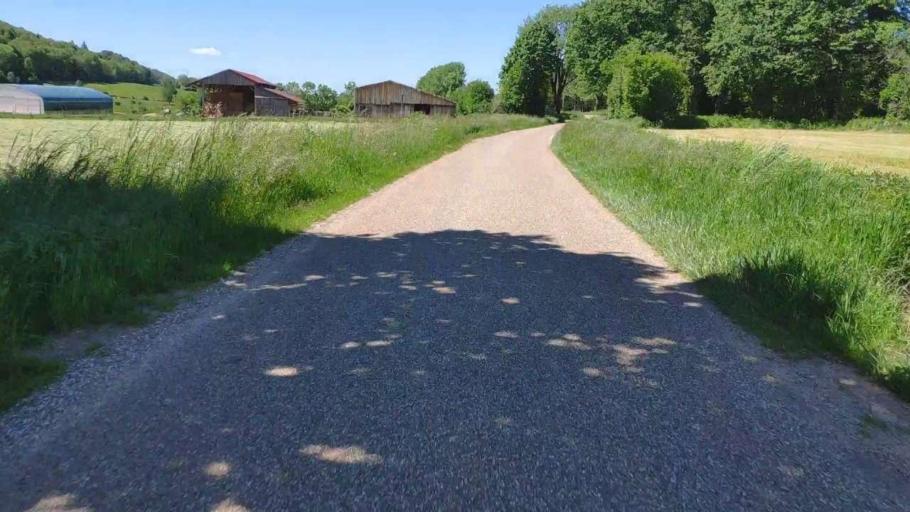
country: FR
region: Franche-Comte
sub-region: Departement du Jura
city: Poligny
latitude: 46.7304
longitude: 5.7540
